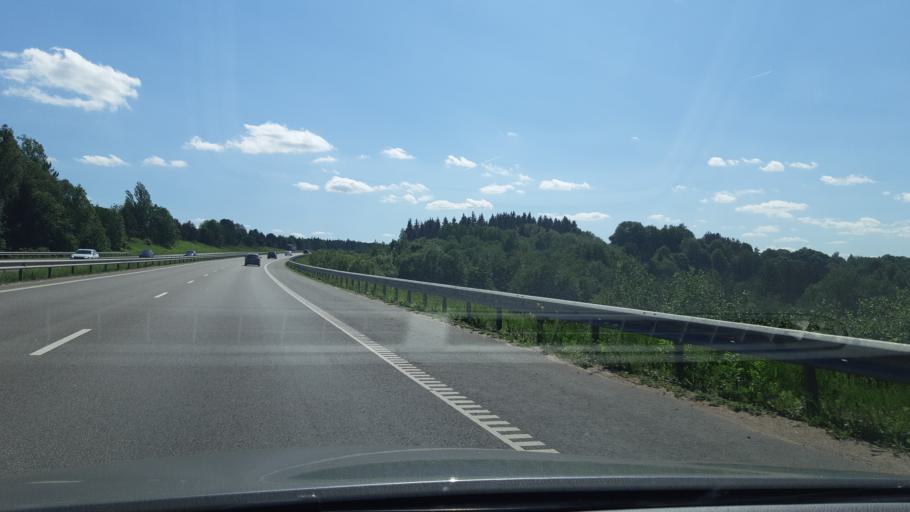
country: LT
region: Kauno apskritis
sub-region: Kauno rajonas
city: Karmelava
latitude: 54.9853
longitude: 24.1072
